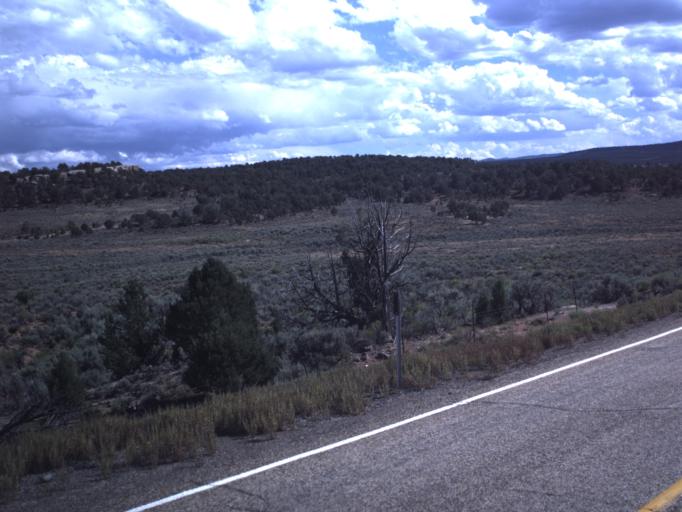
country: US
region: Utah
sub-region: Duchesne County
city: Duchesne
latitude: 40.2445
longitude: -110.7131
